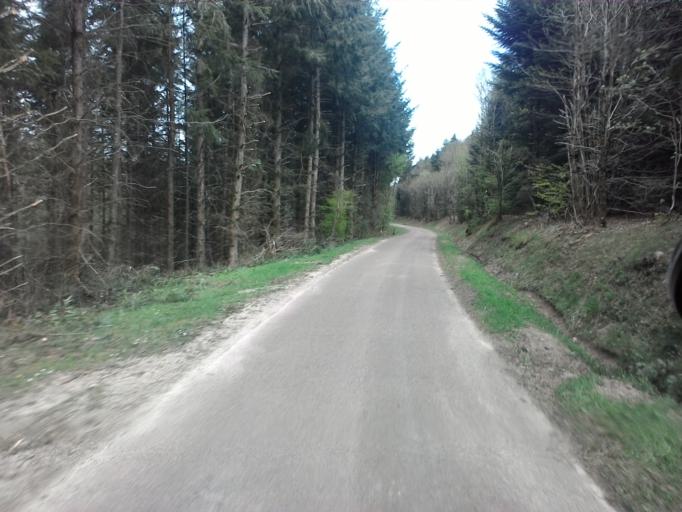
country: FR
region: Bourgogne
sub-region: Departement de la Nievre
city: Lormes
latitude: 47.3226
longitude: 3.8970
